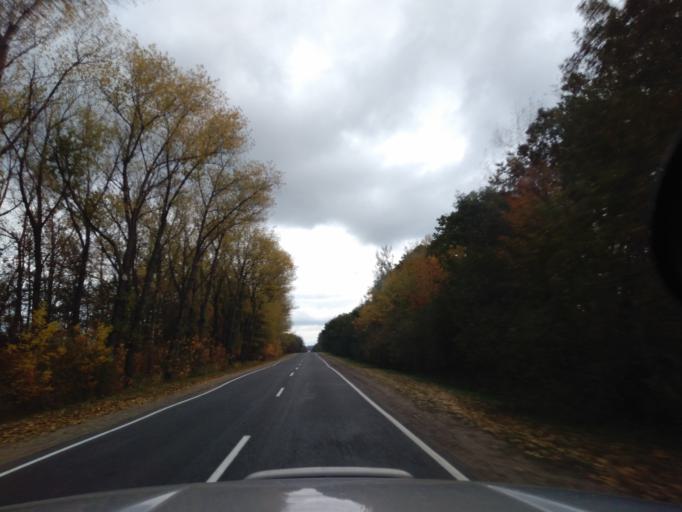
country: BY
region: Minsk
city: Slutsk
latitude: 53.2229
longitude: 27.3646
